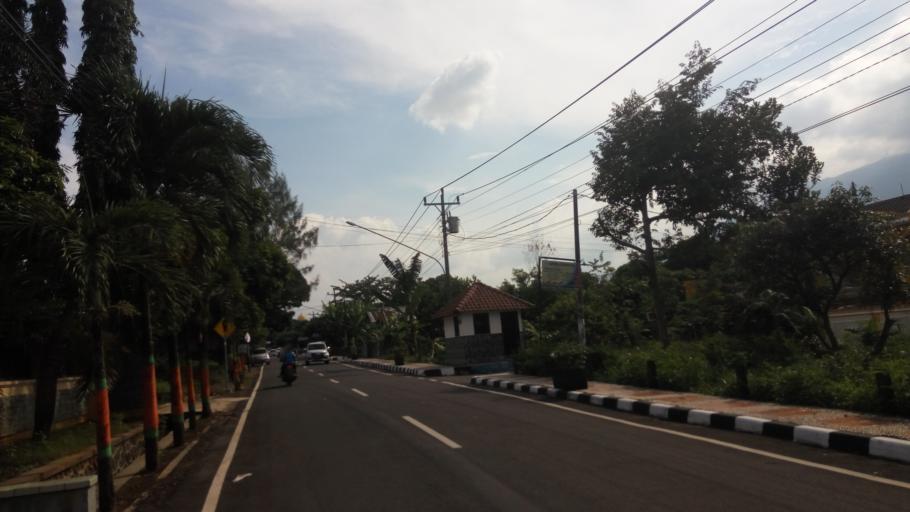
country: ID
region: Central Java
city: Ungaran
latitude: -7.1309
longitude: 110.4123
